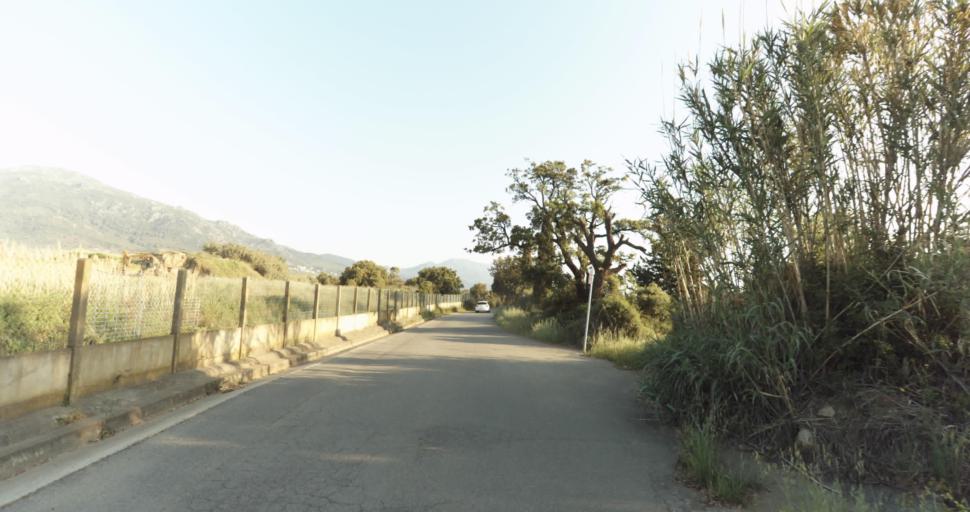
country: FR
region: Corsica
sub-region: Departement de la Haute-Corse
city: Biguglia
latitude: 42.6043
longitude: 9.4446
